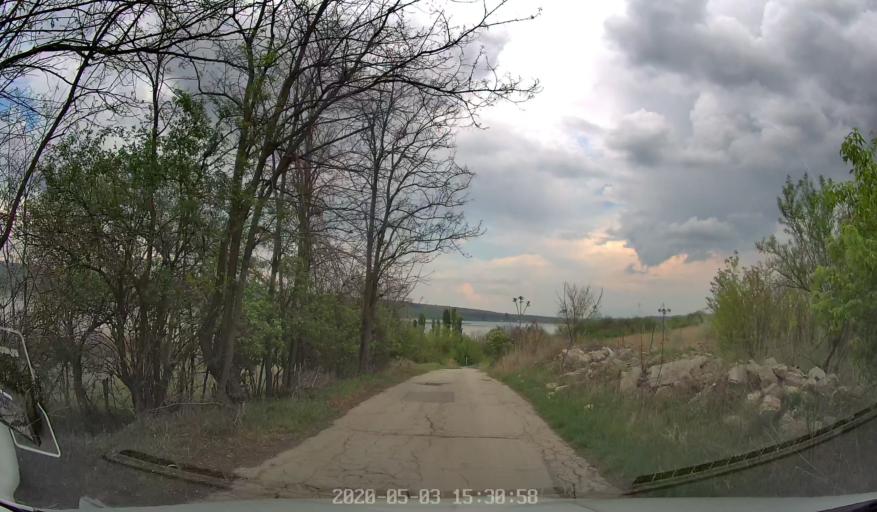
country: MD
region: Chisinau
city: Vatra
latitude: 47.0979
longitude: 28.7056
